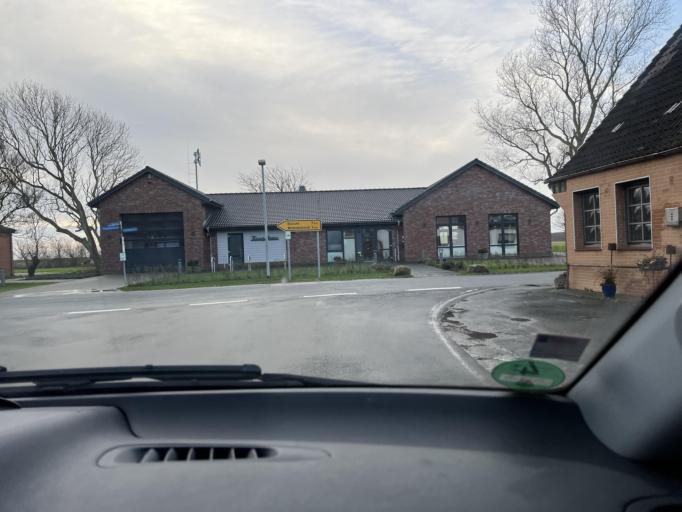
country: DE
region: Schleswig-Holstein
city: Hedwigenkoog
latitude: 54.1781
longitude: 8.8415
